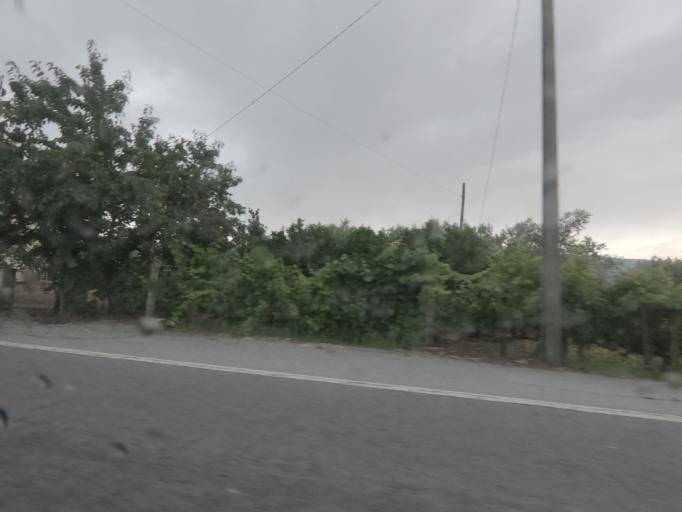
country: PT
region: Vila Real
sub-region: Peso da Regua
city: Peso da Regua
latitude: 41.1324
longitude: -7.7518
